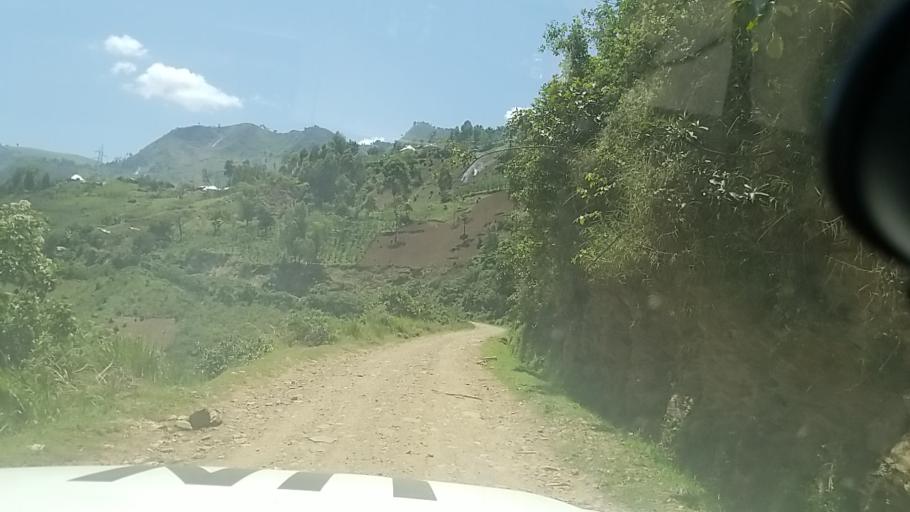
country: CD
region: Nord Kivu
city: Sake
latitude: -1.9124
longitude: 28.9653
